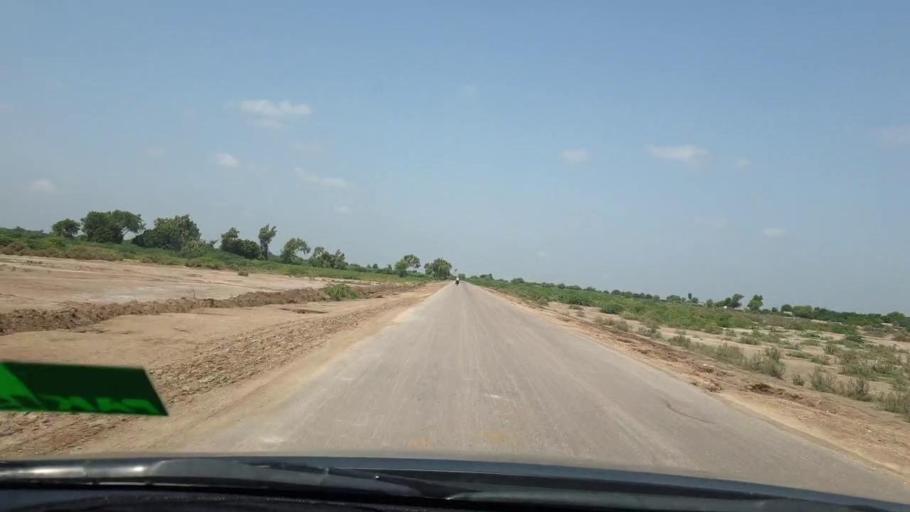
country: PK
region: Sindh
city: Digri
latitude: 24.9926
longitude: 69.1249
